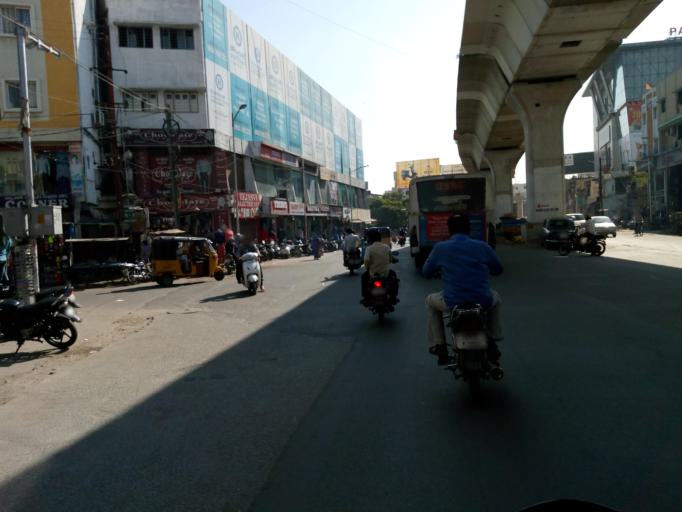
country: IN
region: Telangana
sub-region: Hyderabad
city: Hyderabad
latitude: 17.3917
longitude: 78.4892
